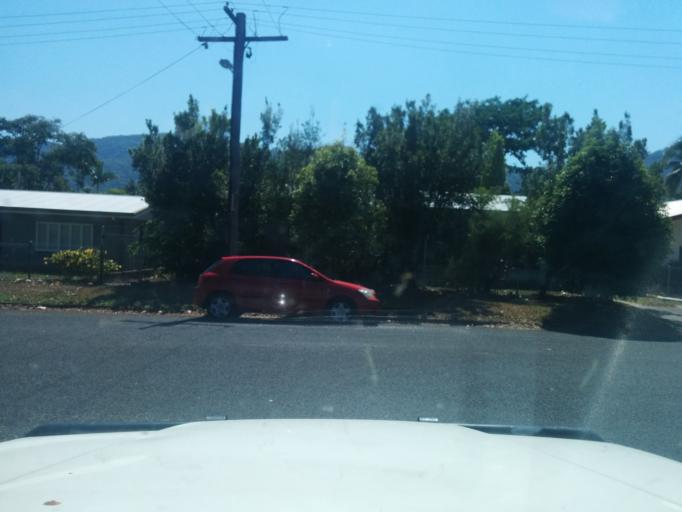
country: AU
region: Queensland
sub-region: Cairns
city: Woree
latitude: -16.9448
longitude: 145.7359
